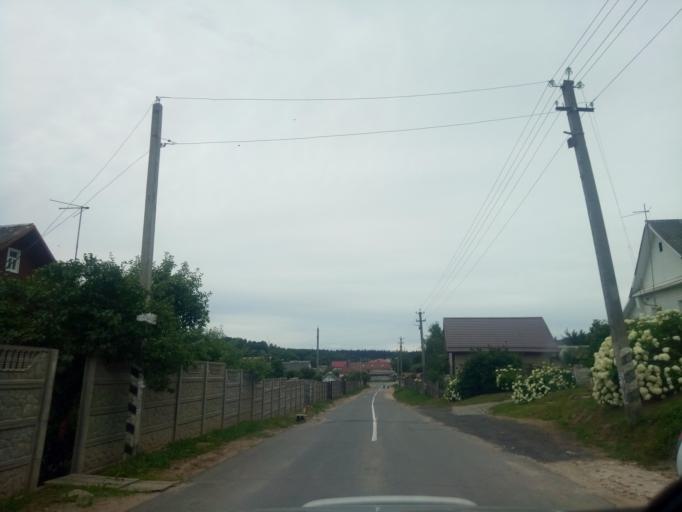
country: BY
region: Minsk
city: Zhdanovichy
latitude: 53.9259
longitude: 27.3839
